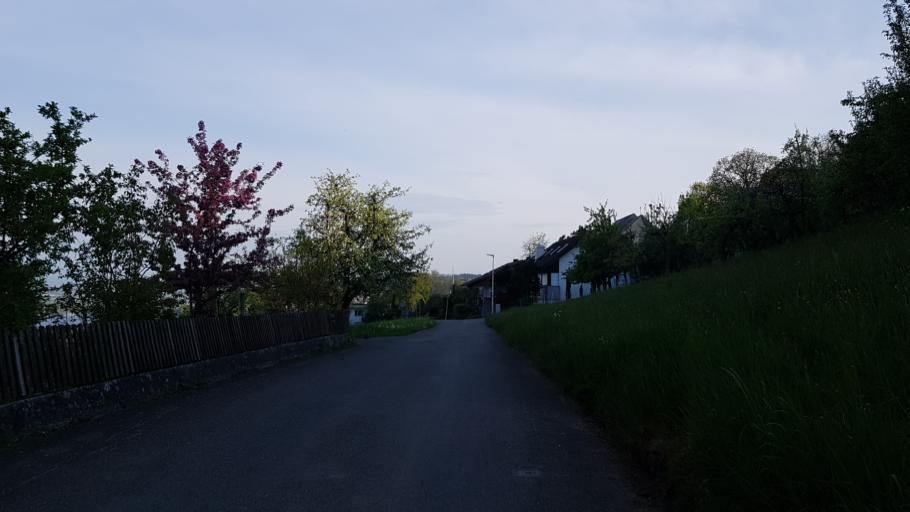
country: CH
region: Aargau
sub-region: Bezirk Kulm
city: Reinach
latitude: 47.2771
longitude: 8.1980
